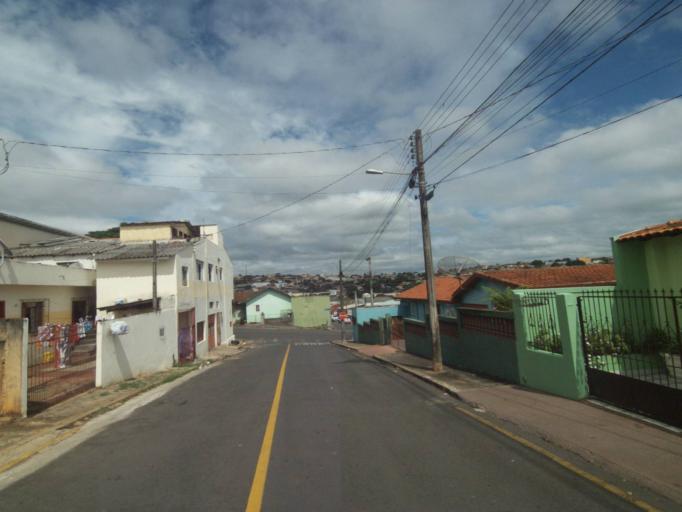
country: BR
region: Parana
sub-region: Telemaco Borba
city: Telemaco Borba
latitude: -24.3279
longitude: -50.6297
